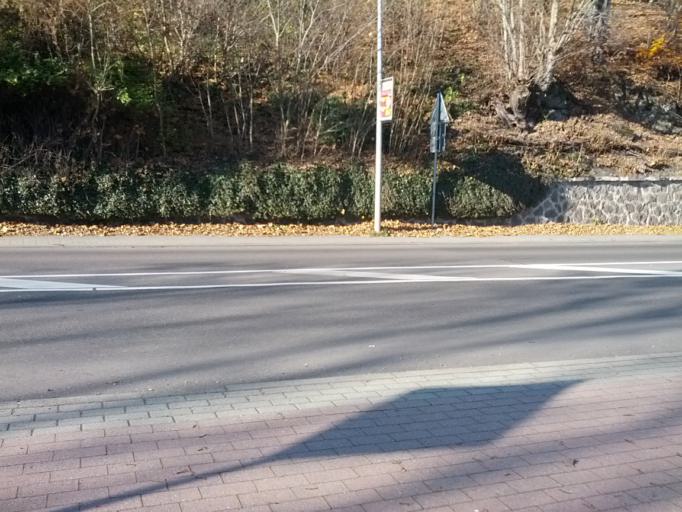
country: DE
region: Thuringia
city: Thal
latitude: 50.9210
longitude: 10.3947
